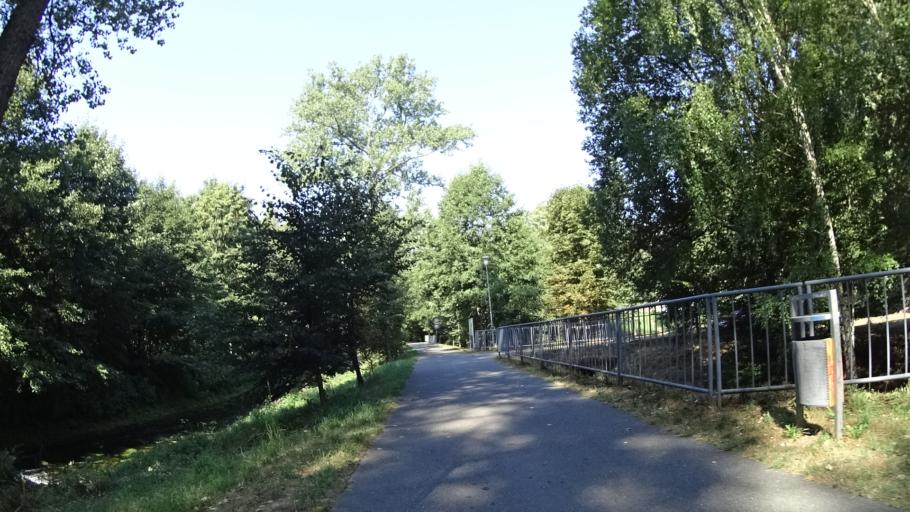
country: CZ
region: Liberecky
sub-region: Okres Liberec
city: Liberec
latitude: 50.7797
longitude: 15.0475
